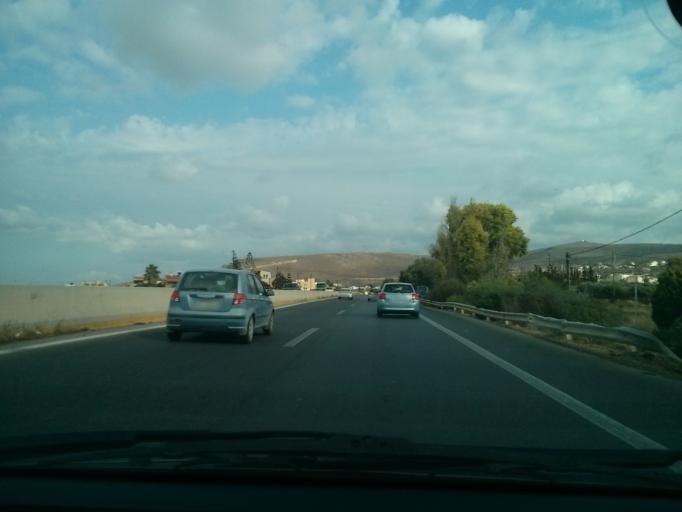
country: GR
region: Crete
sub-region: Nomos Irakleiou
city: Kokkini Hani
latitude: 35.3294
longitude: 25.2466
